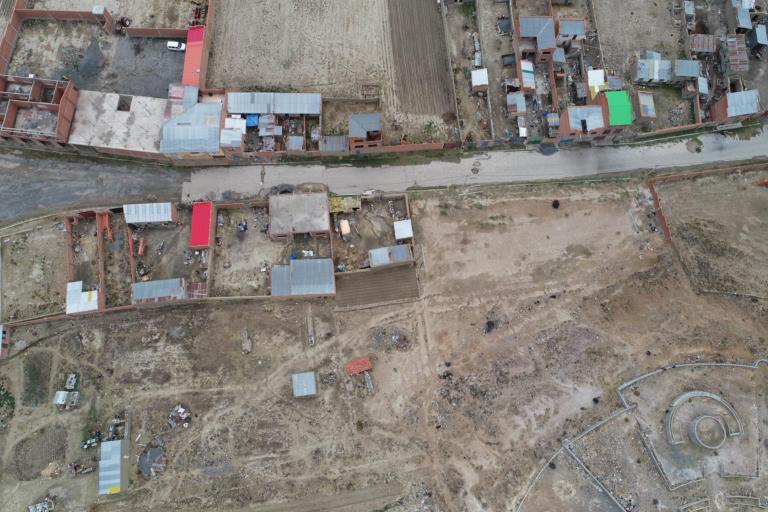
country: BO
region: La Paz
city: Achacachi
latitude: -16.0520
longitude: -68.6826
